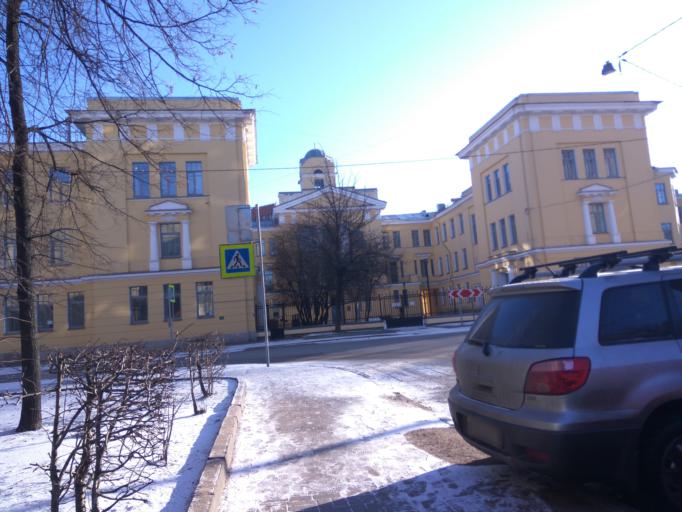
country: RU
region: St.-Petersburg
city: Petrogradka
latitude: 59.9737
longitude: 30.3106
